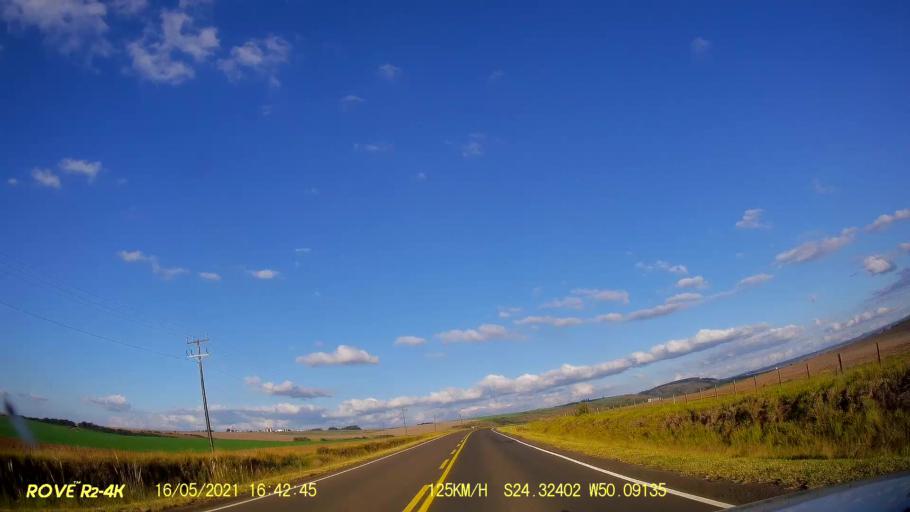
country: BR
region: Parana
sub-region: Pirai Do Sul
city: Pirai do Sul
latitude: -24.3246
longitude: -50.0915
